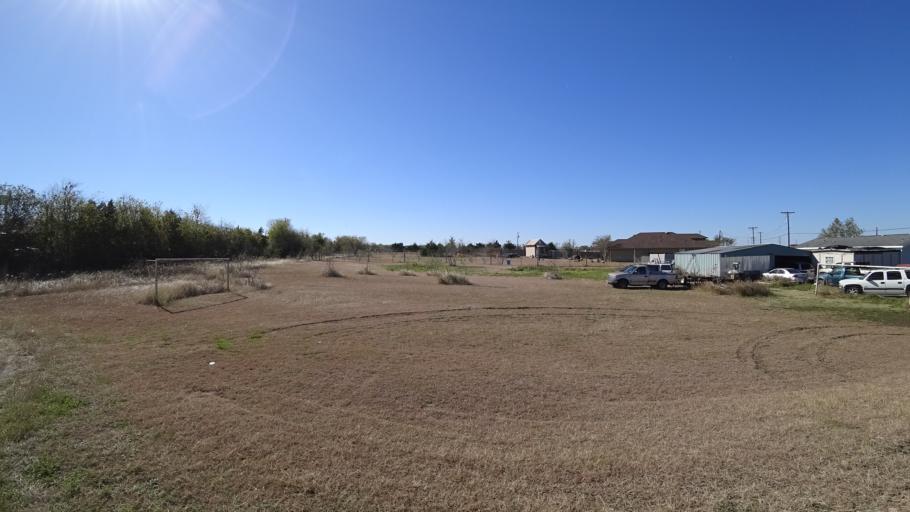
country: US
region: Texas
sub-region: Travis County
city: Garfield
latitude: 30.1037
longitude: -97.6004
